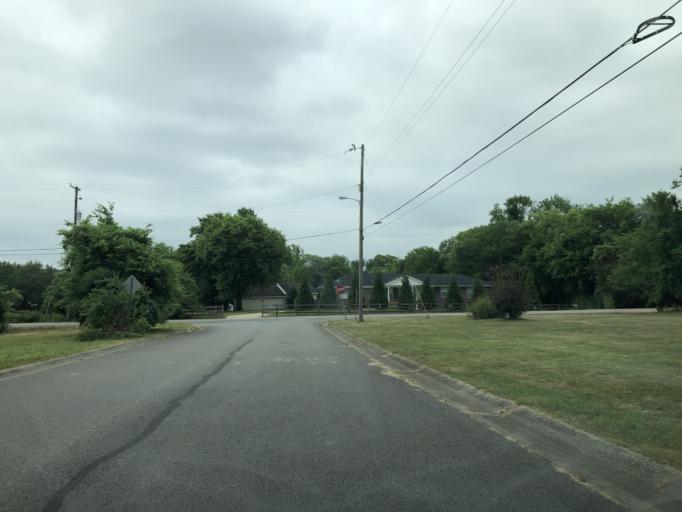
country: US
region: Tennessee
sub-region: Davidson County
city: Goodlettsville
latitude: 36.2903
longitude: -86.7459
